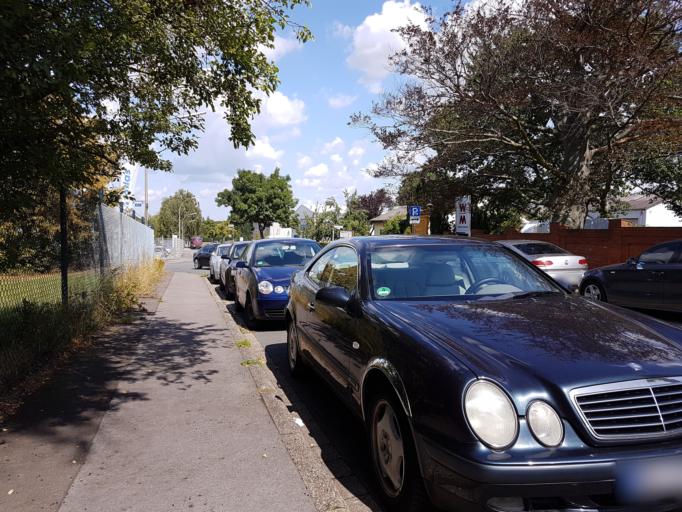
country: DE
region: North Rhine-Westphalia
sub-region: Regierungsbezirk Arnsberg
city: Holzwickede
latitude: 51.5317
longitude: 7.6310
